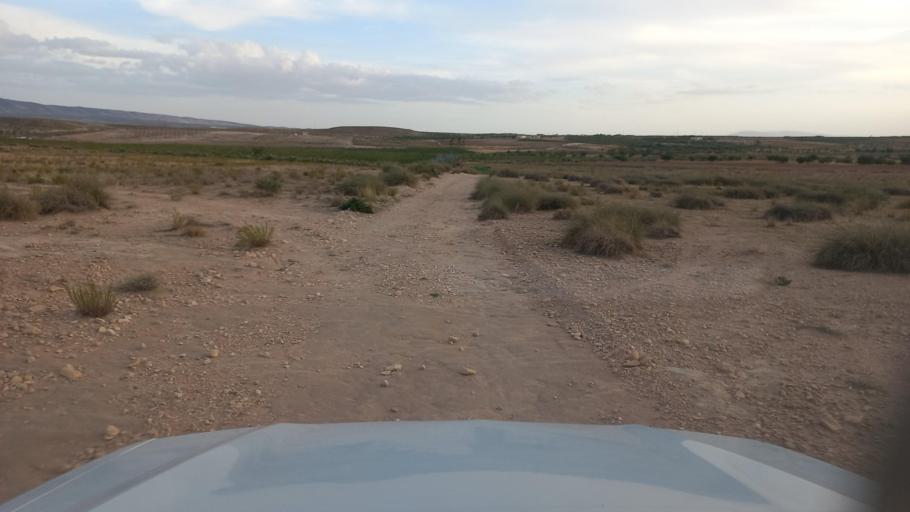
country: TN
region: Al Qasrayn
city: Sbiba
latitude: 35.4172
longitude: 9.0880
